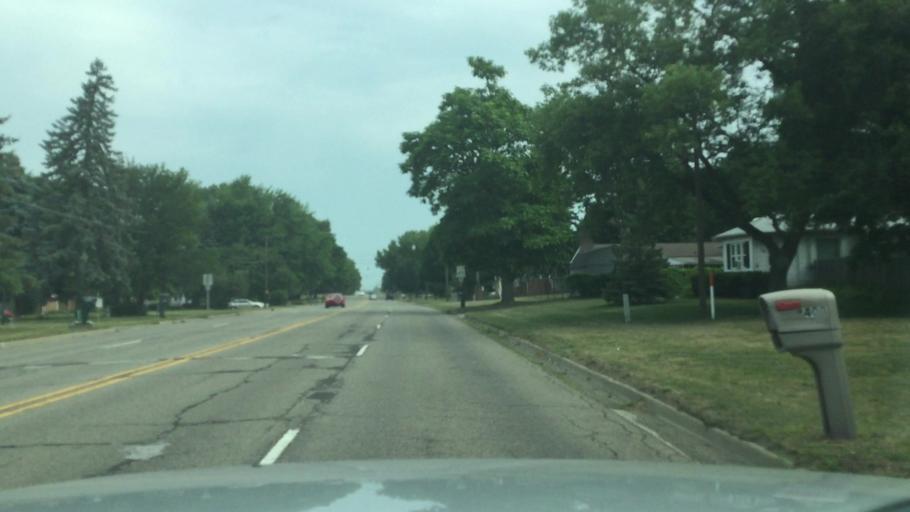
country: US
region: Michigan
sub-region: Genesee County
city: Flint
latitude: 42.9625
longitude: -83.7124
